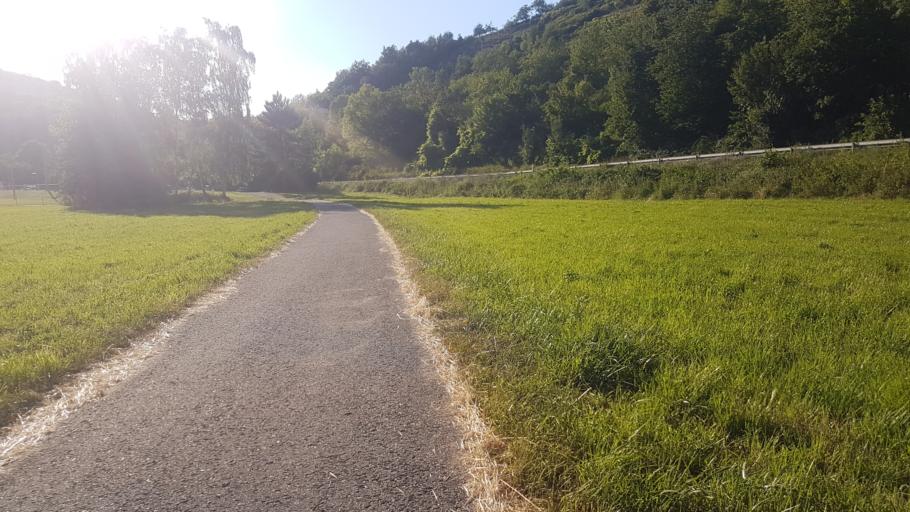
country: DE
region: Baden-Wuerttemberg
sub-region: Regierungsbezirk Stuttgart
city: Neudenau
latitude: 49.3031
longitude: 9.3126
